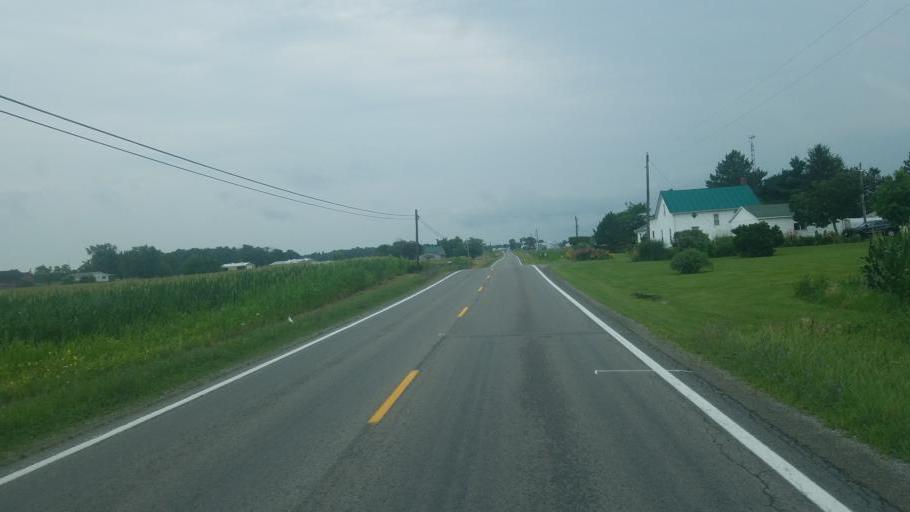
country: US
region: Ohio
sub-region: Hardin County
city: Kenton
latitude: 40.6196
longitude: -83.6609
